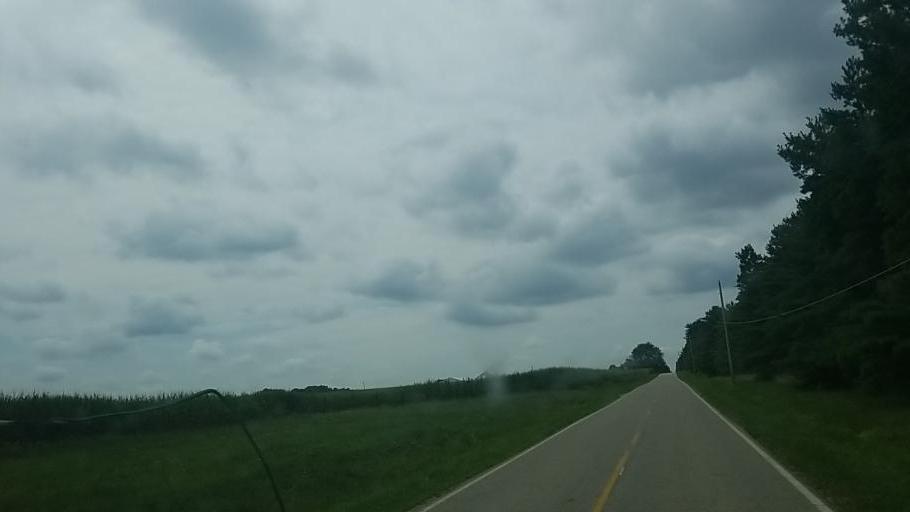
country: US
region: Ohio
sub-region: Fairfield County
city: Lithopolis
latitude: 39.7523
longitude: -82.8517
